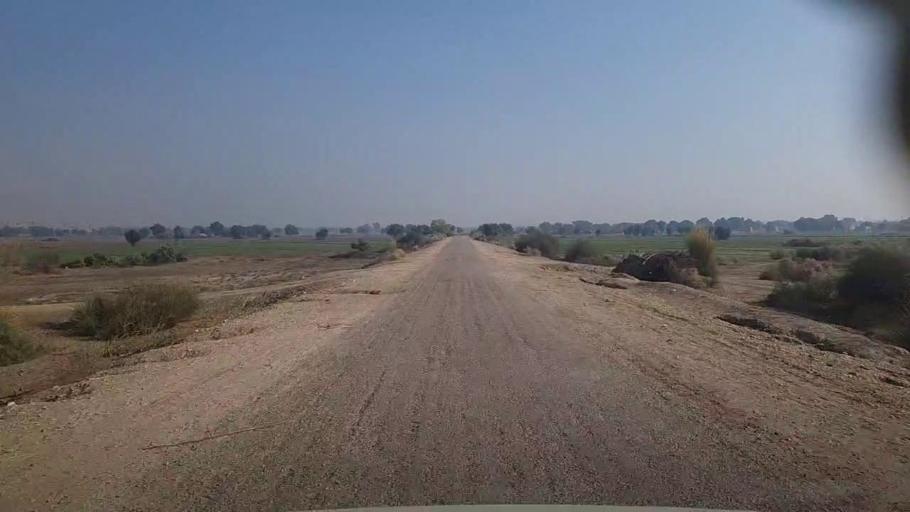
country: PK
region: Sindh
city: Kandiari
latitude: 26.8211
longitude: 68.4918
